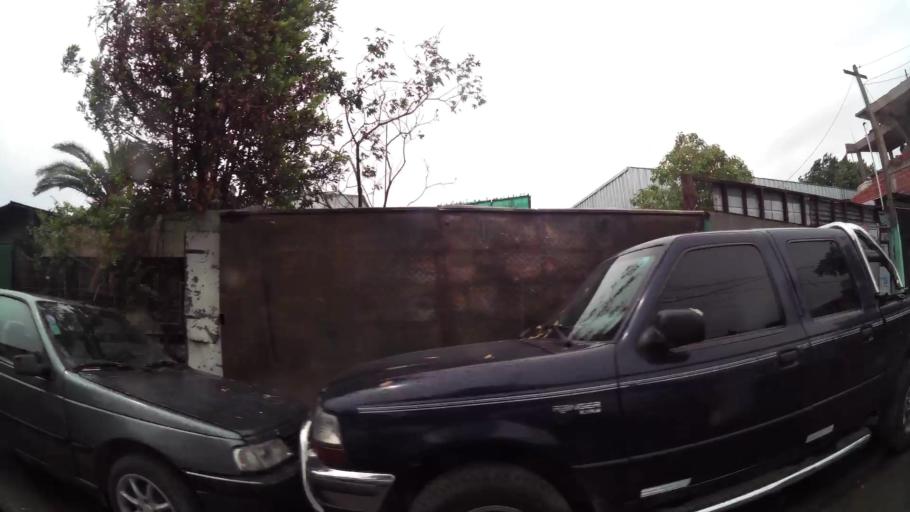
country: AR
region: Buenos Aires F.D.
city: Villa Lugano
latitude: -34.6564
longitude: -58.4423
